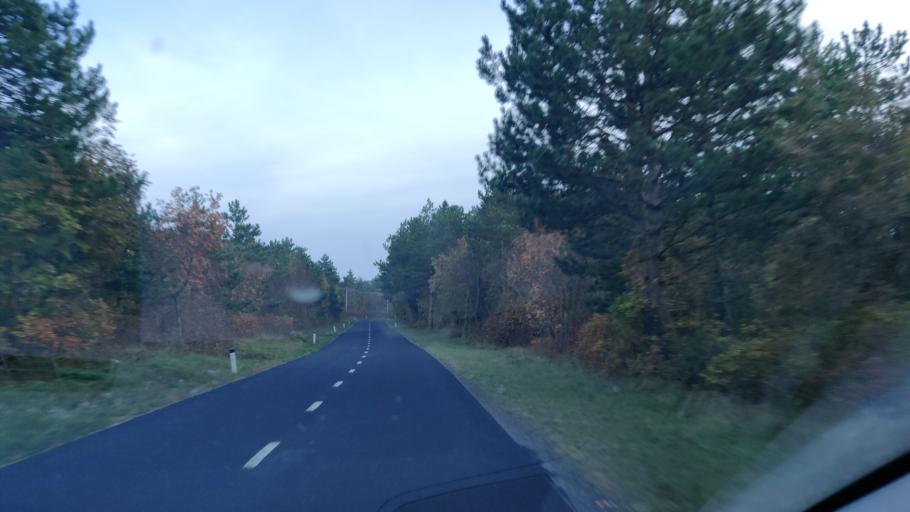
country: SI
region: Sezana
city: Sezana
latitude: 45.7488
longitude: 13.9246
